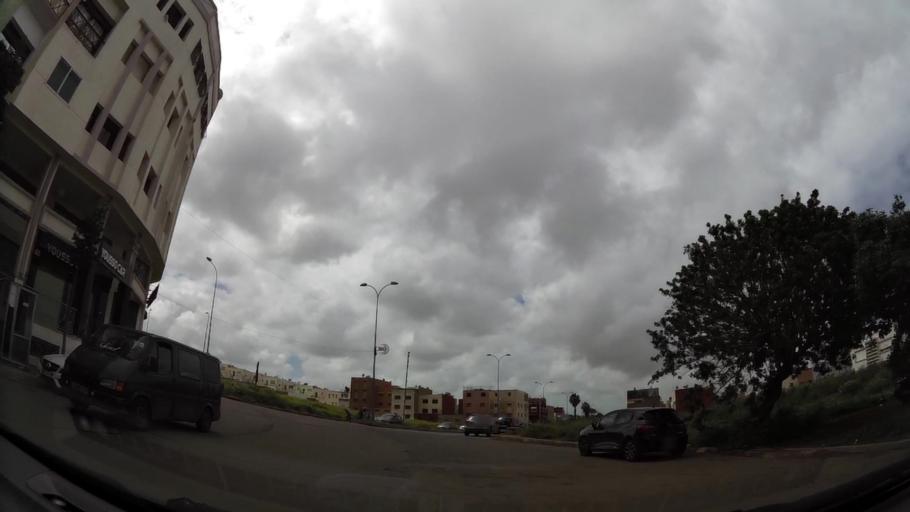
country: MA
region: Grand Casablanca
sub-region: Casablanca
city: Casablanca
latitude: 33.5339
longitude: -7.5980
